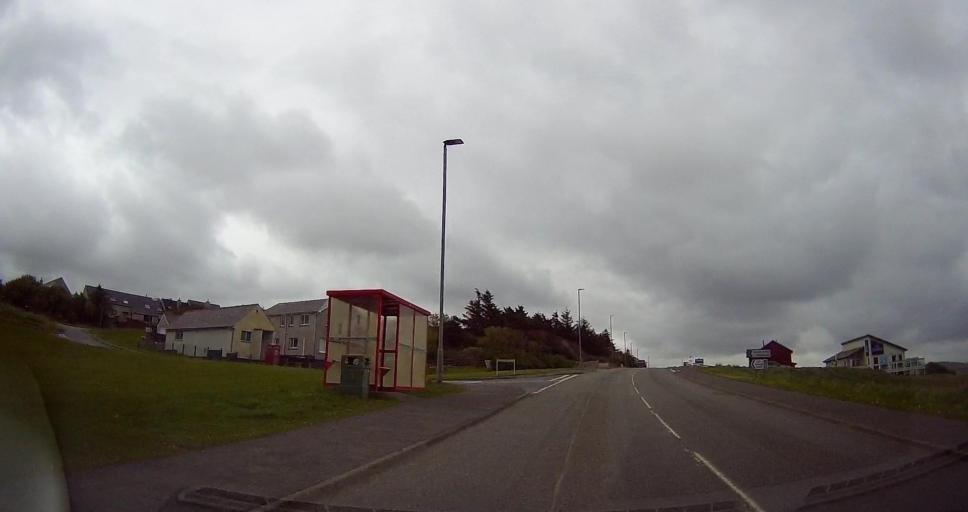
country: GB
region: Scotland
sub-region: Shetland Islands
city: Lerwick
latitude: 60.3940
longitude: -1.3516
